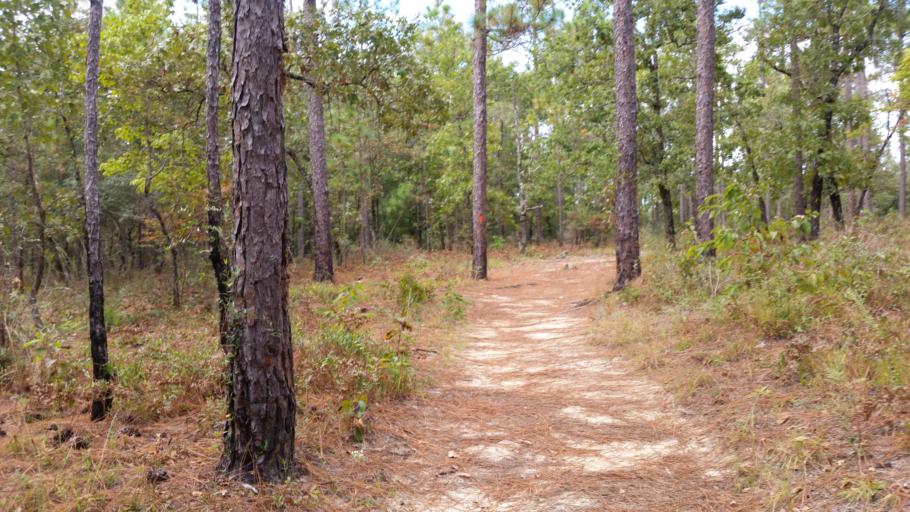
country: US
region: Florida
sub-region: Santa Rosa County
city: Point Baker
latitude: 30.8622
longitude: -86.8450
